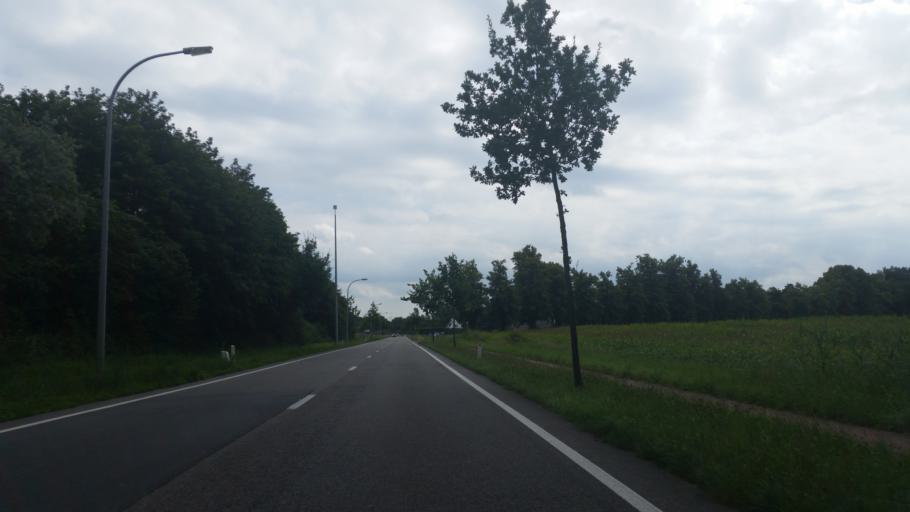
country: BE
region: Flanders
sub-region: Provincie Antwerpen
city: Merksplas
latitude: 51.3810
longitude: 4.8278
